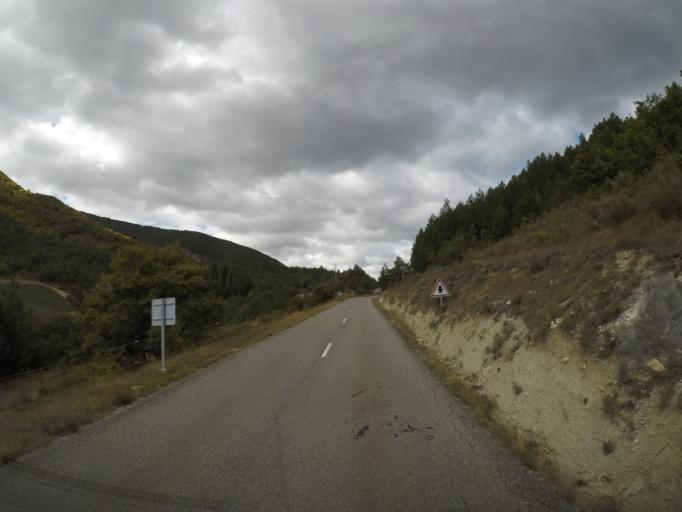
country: FR
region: Provence-Alpes-Cote d'Azur
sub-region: Departement du Vaucluse
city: Sault
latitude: 44.1792
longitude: 5.5707
